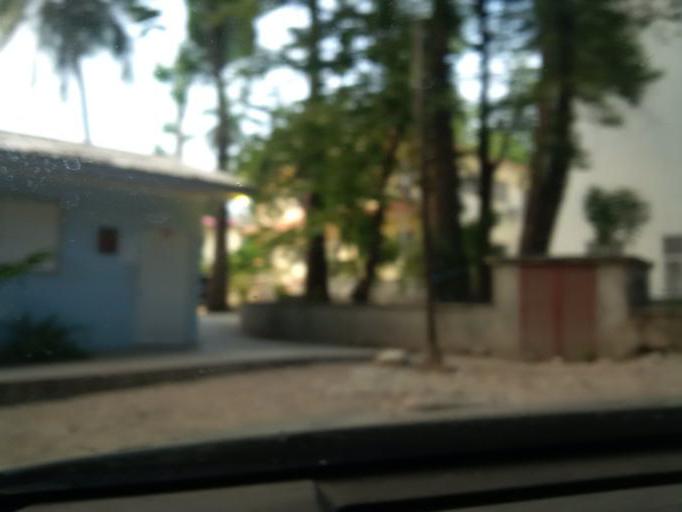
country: HT
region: Ouest
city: Port-au-Prince
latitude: 18.5255
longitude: -72.3217
